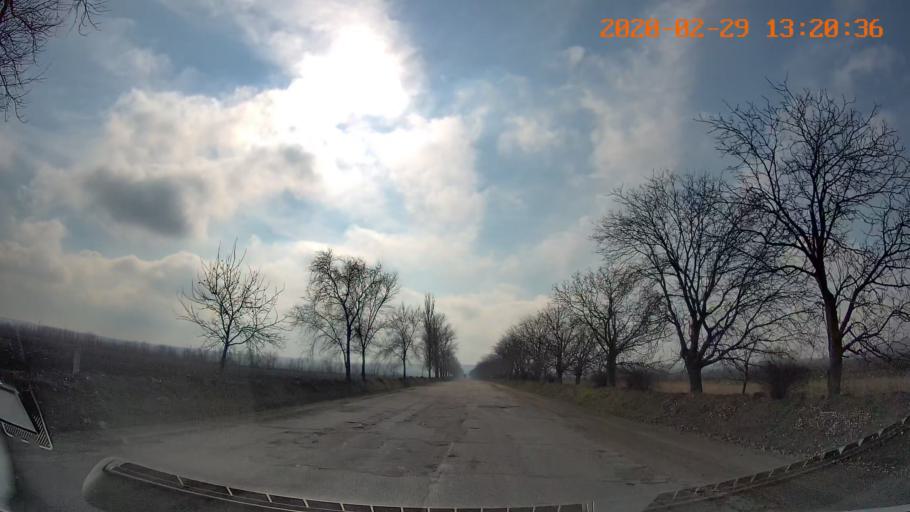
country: MD
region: Telenesti
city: Camenca
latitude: 47.9774
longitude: 28.6400
